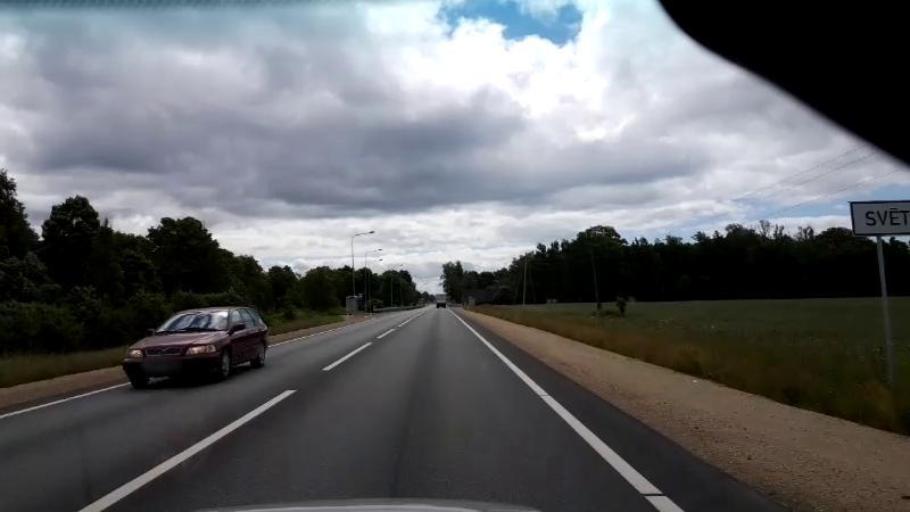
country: LV
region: Salacgrivas
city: Salacgriva
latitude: 57.7018
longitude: 24.3720
